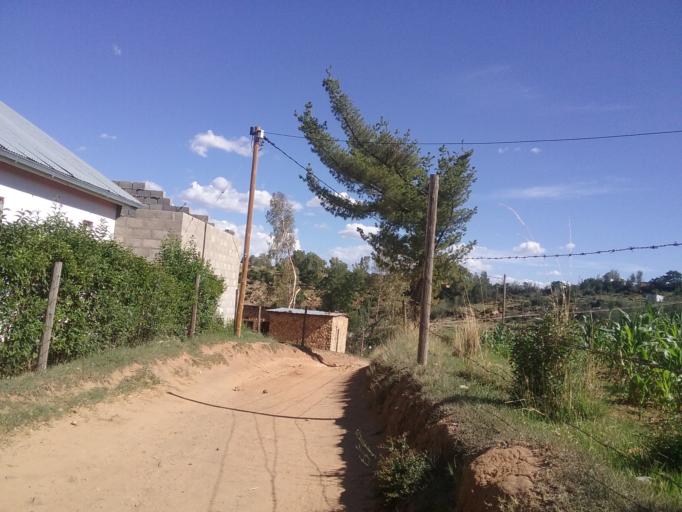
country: LS
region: Maseru
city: Maseru
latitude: -29.4184
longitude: 27.5695
